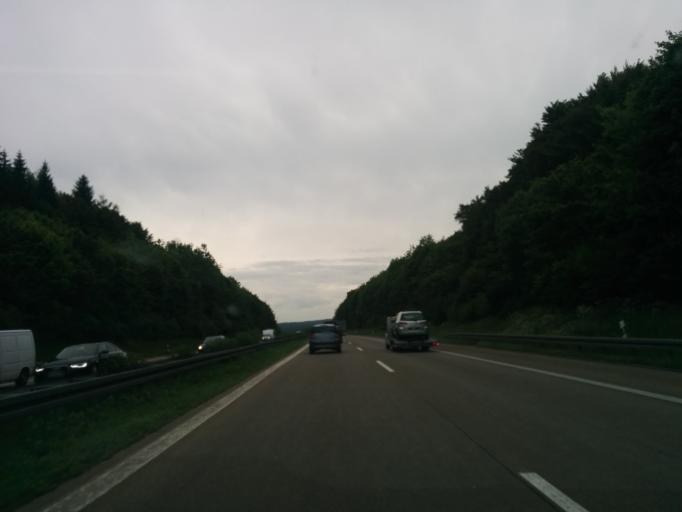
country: DE
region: Baden-Wuerttemberg
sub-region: Regierungsbezirk Stuttgart
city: Nattheim
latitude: 48.7735
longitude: 10.2112
